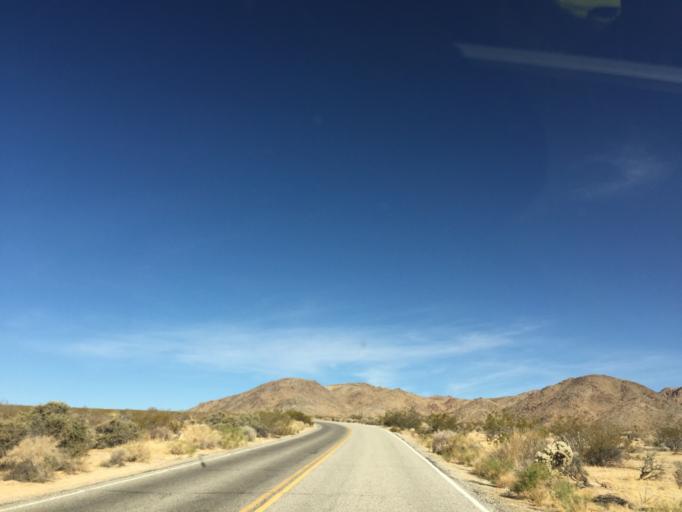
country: US
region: California
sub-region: San Bernardino County
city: Twentynine Palms
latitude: 33.9726
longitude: -115.9967
